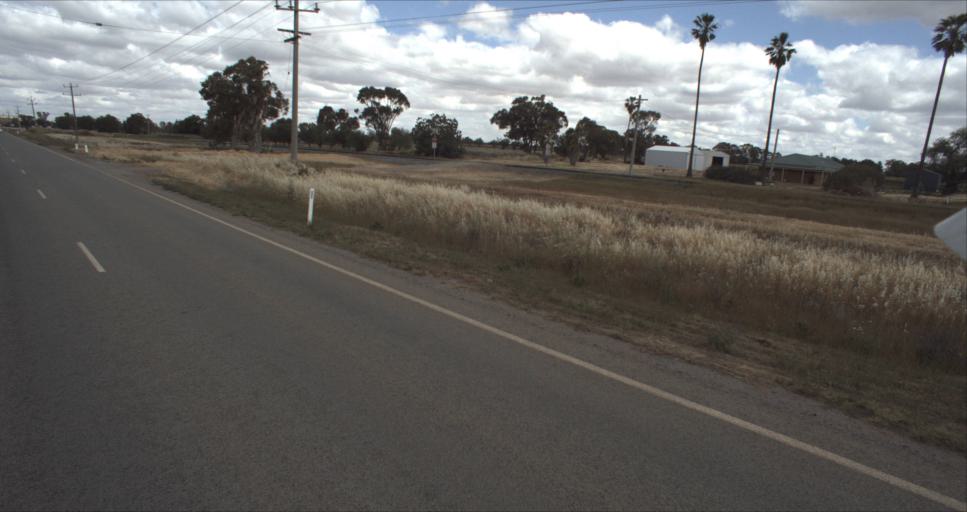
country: AU
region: New South Wales
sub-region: Leeton
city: Leeton
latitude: -34.5871
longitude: 146.4038
